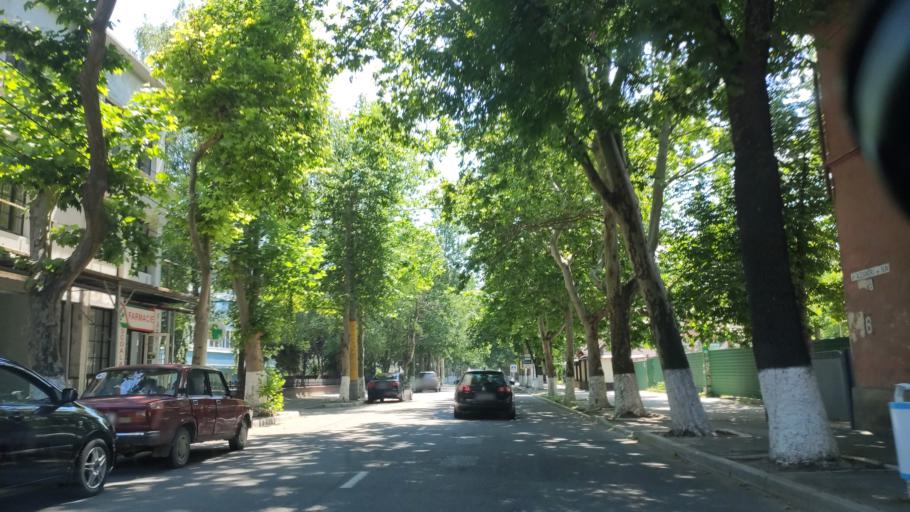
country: MD
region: Raionul Soroca
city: Soroca
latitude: 48.1559
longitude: 28.3001
